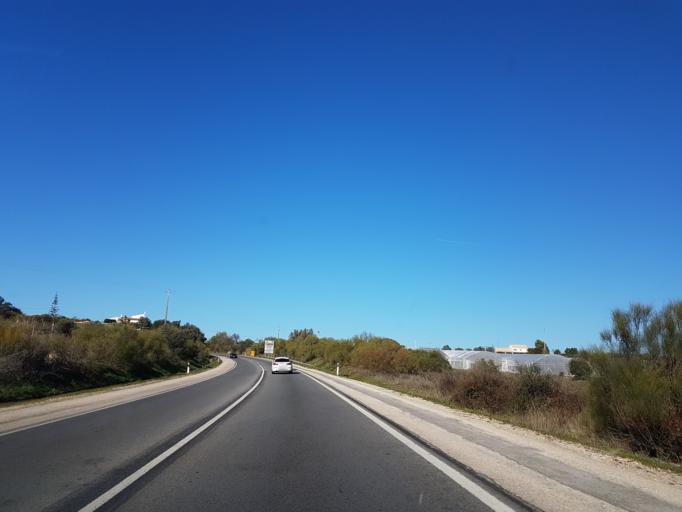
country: PT
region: Faro
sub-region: Lagoa
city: Estombar
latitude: 37.1495
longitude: -8.4800
